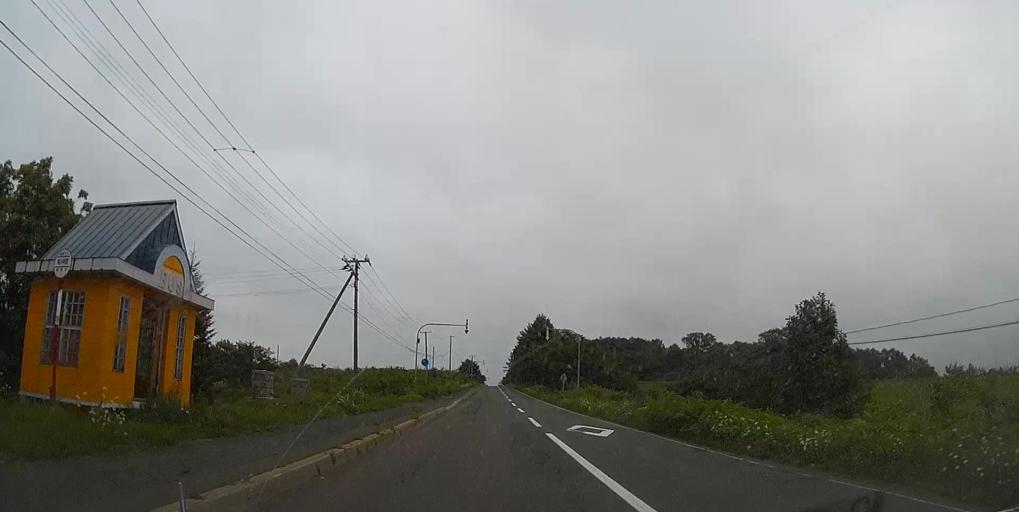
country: JP
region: Hokkaido
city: Iwanai
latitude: 42.4348
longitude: 139.9796
